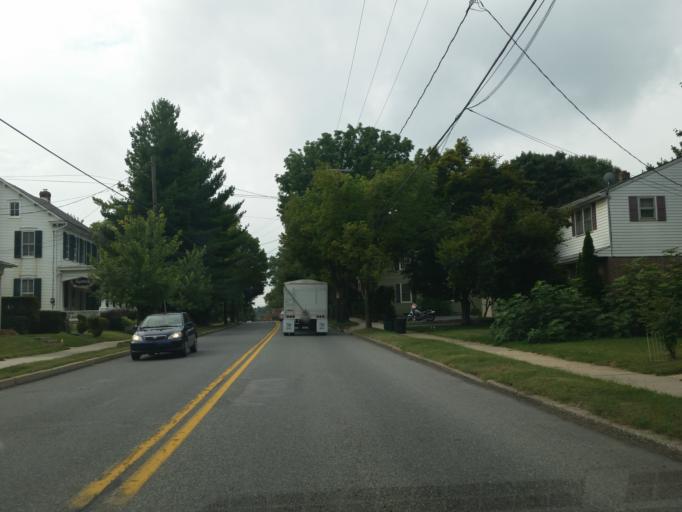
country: US
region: Pennsylvania
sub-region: Lancaster County
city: Lititz
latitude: 40.1628
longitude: -76.3079
